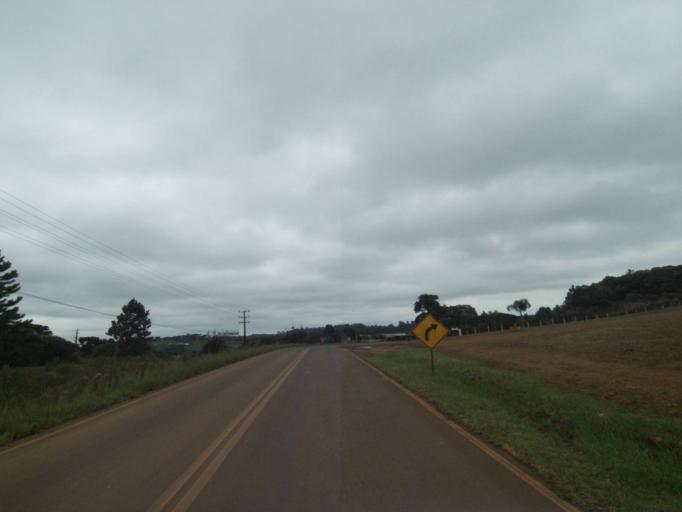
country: BR
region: Parana
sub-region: Pitanga
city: Pitanga
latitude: -24.9308
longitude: -51.8757
